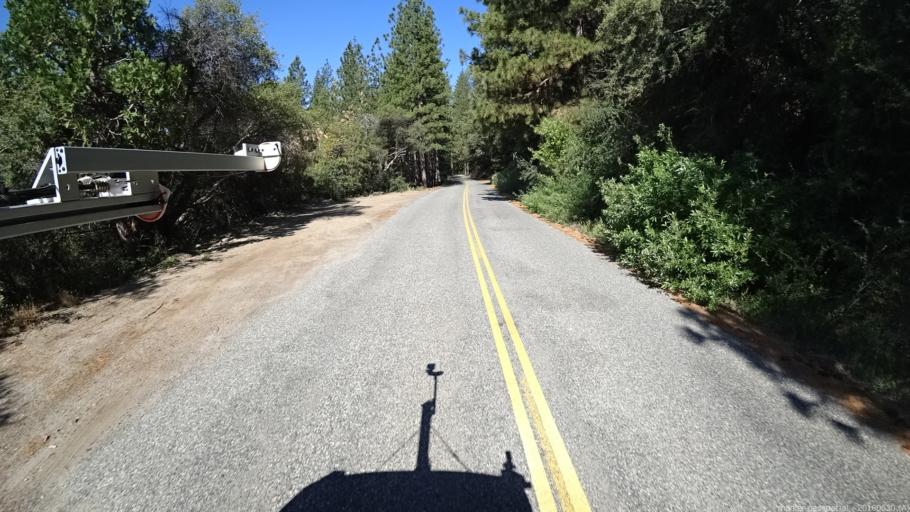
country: US
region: California
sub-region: Fresno County
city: Auberry
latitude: 37.2177
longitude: -119.3743
